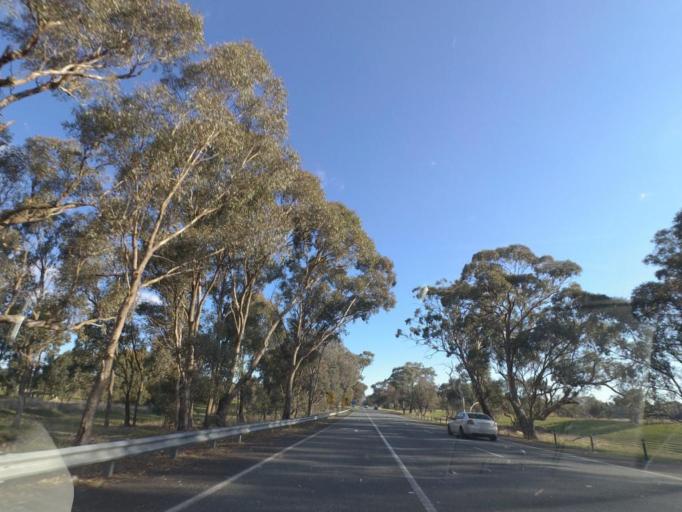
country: AU
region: Victoria
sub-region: Benalla
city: Benalla
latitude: -36.6929
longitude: 145.6605
